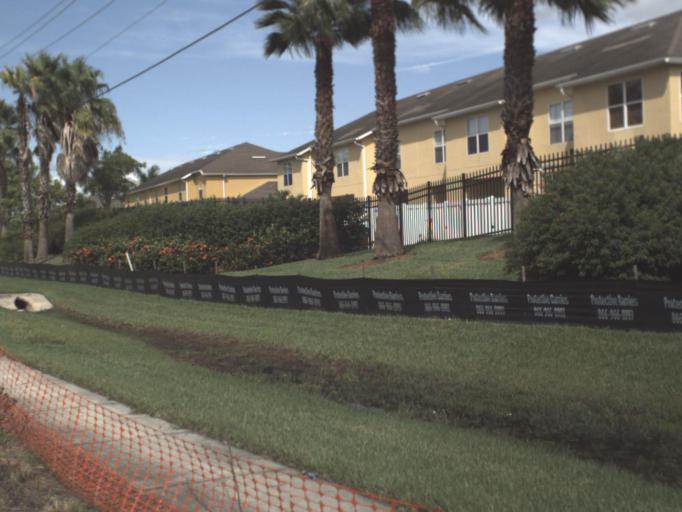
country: US
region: Florida
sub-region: Lee County
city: Fort Myers
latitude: 26.6095
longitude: -81.8514
